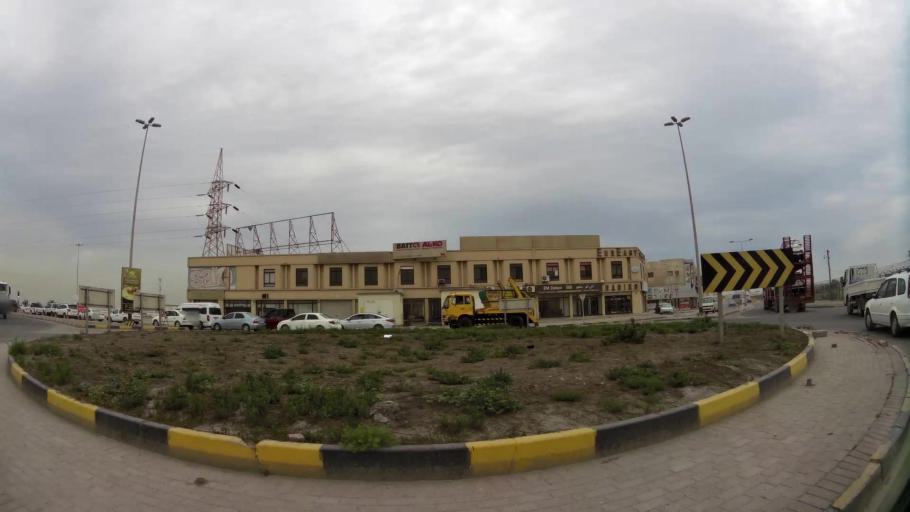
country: BH
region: Northern
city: Sitrah
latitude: 26.1481
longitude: 50.6197
